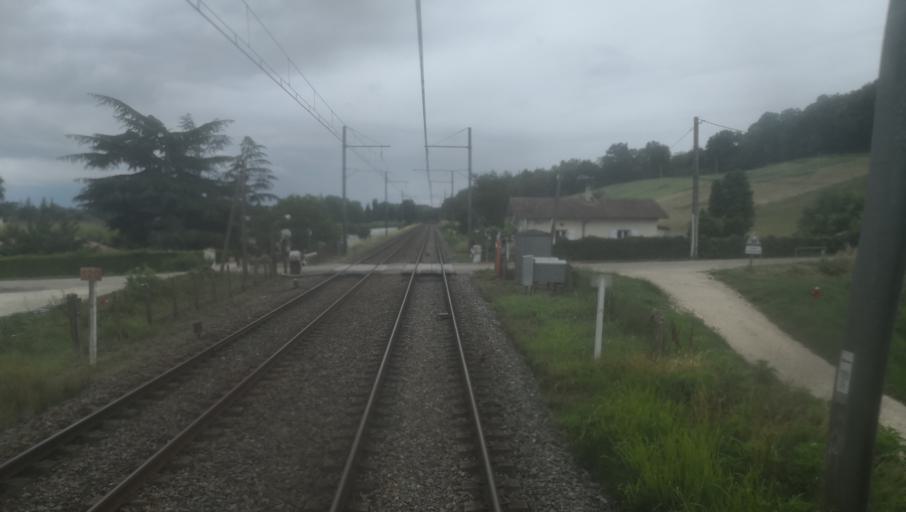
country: FR
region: Aquitaine
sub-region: Departement du Lot-et-Garonne
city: Port-Sainte-Marie
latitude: 44.2391
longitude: 0.4405
